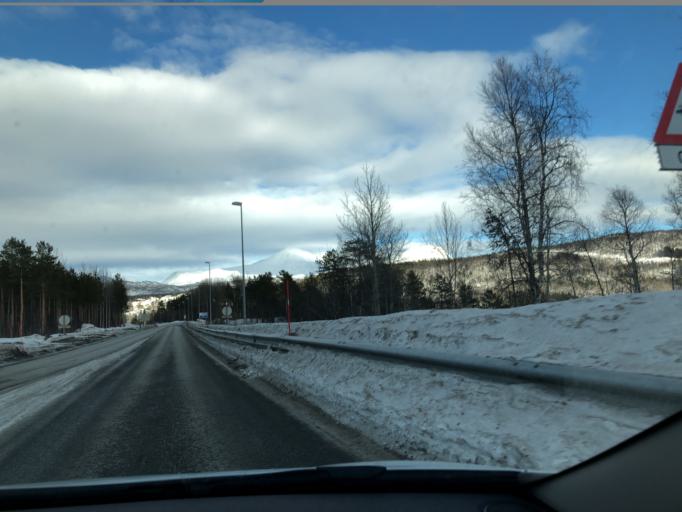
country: NO
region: Troms
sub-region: Malselv
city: Moen
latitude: 69.1332
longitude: 18.5828
